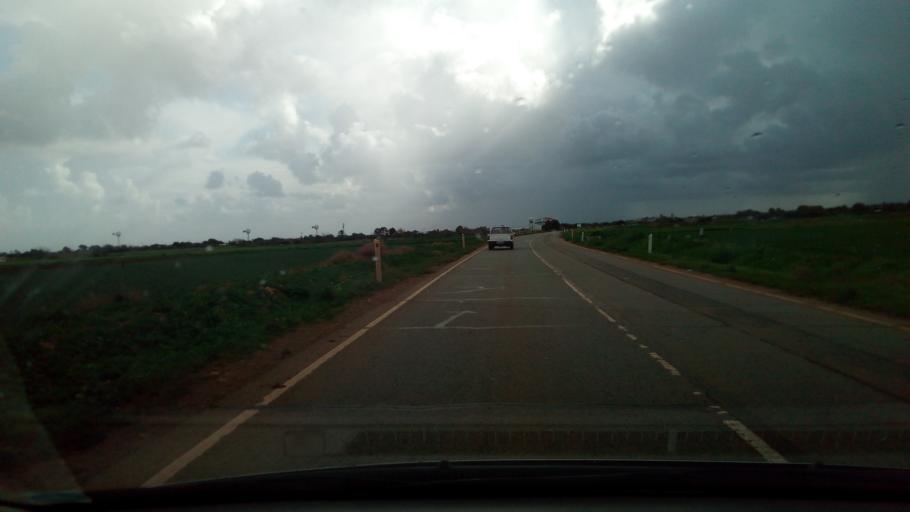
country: CY
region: Ammochostos
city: Liopetri
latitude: 34.9861
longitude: 33.8943
